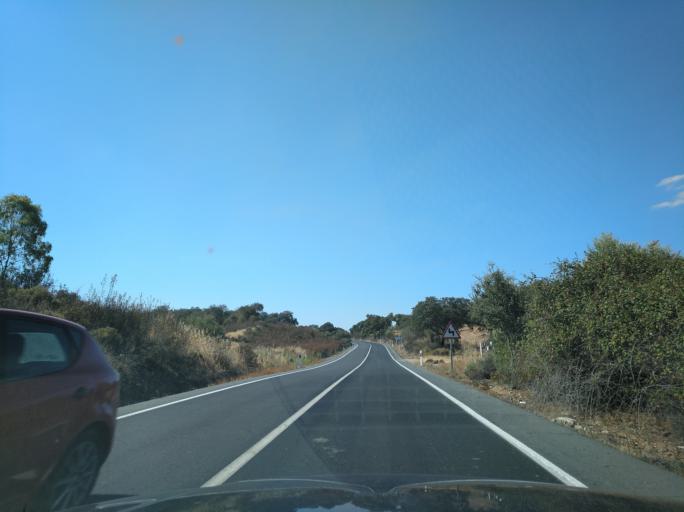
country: ES
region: Andalusia
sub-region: Provincia de Huelva
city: Alosno
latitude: 37.5171
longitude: -7.1326
